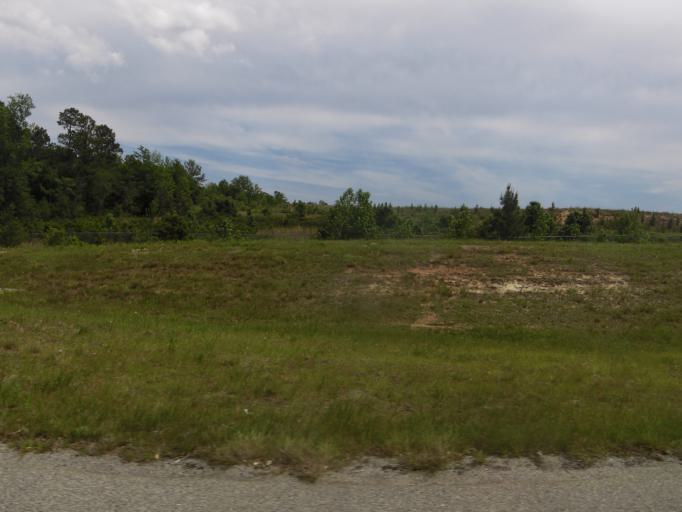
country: US
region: Georgia
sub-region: Emanuel County
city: Swainsboro
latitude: 32.6170
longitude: -82.3800
